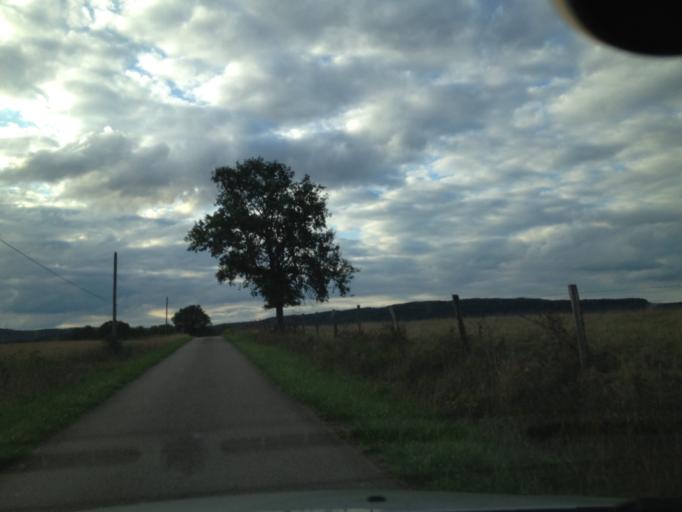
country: FR
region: Lorraine
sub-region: Departement des Vosges
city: Bains-les-Bains
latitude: 47.9837
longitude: 6.1961
